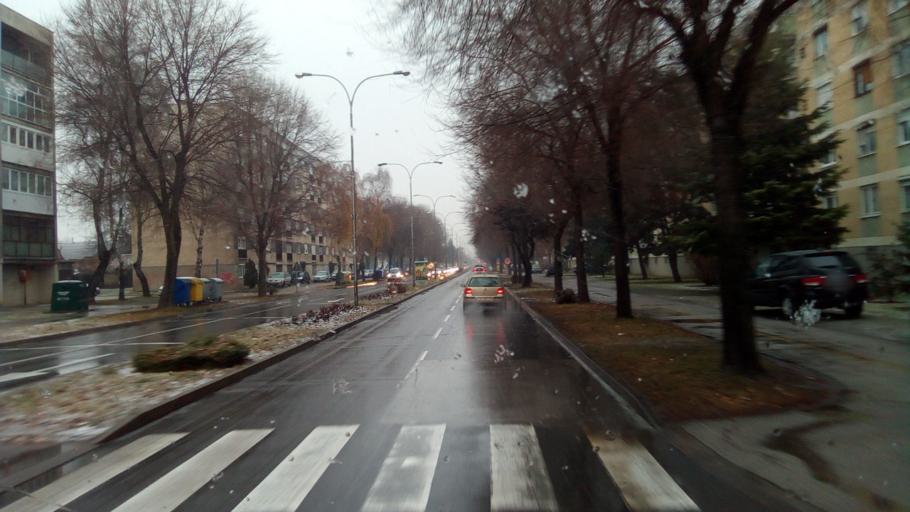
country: HR
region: Varazdinska
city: Varazdin
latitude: 46.2991
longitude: 16.3368
